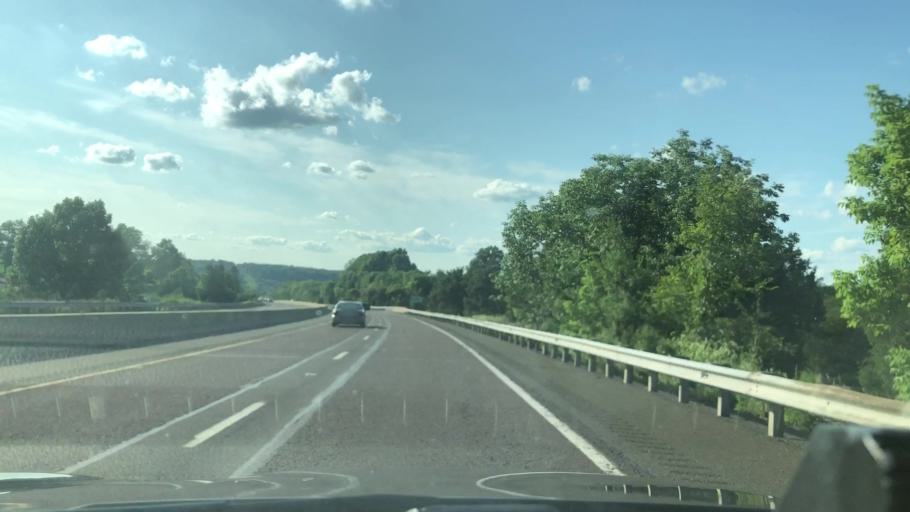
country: US
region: Pennsylvania
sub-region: Bucks County
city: Sellersville
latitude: 40.3418
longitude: -75.3165
